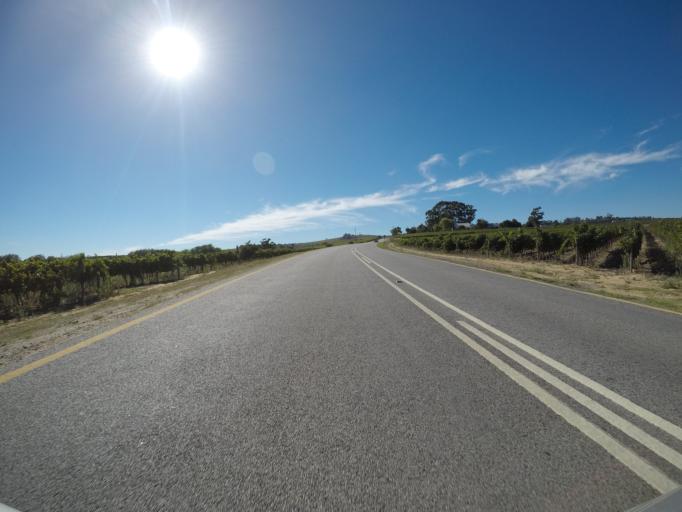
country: ZA
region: Western Cape
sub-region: Cape Winelands District Municipality
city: Stellenbosch
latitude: -33.9740
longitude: 18.7495
